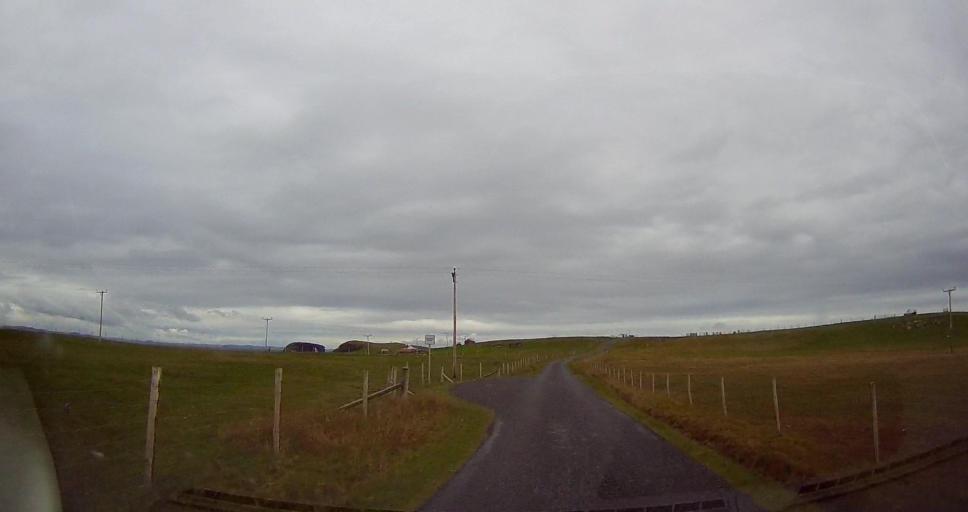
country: GB
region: Scotland
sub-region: Shetland Islands
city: Lerwick
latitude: 60.4830
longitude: -1.6083
